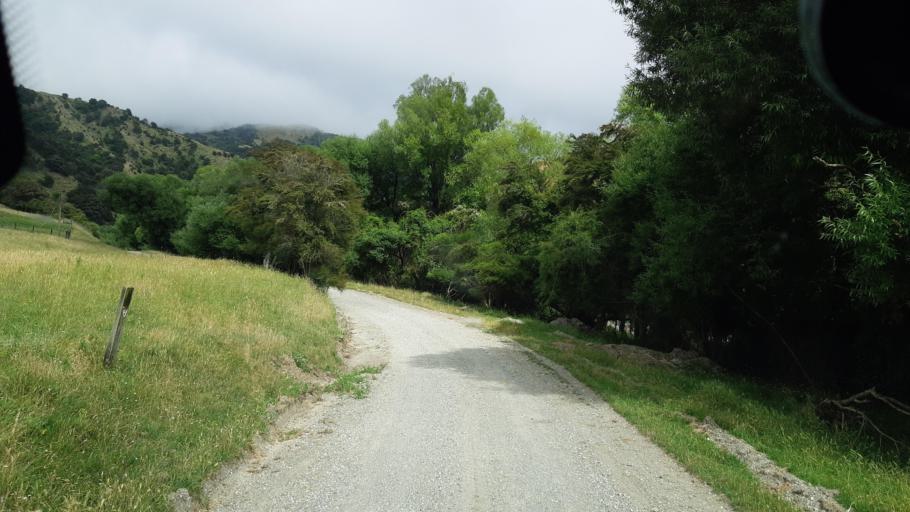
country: NZ
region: Marlborough
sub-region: Marlborough District
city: Blenheim
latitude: -41.9707
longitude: 173.9922
